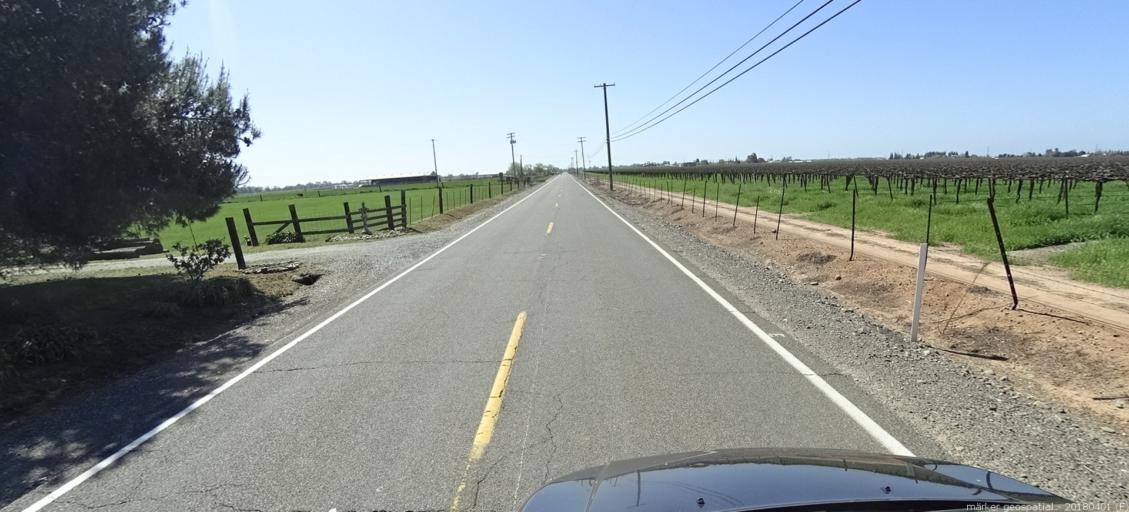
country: US
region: California
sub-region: Sacramento County
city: Herald
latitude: 38.3333
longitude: -121.2238
